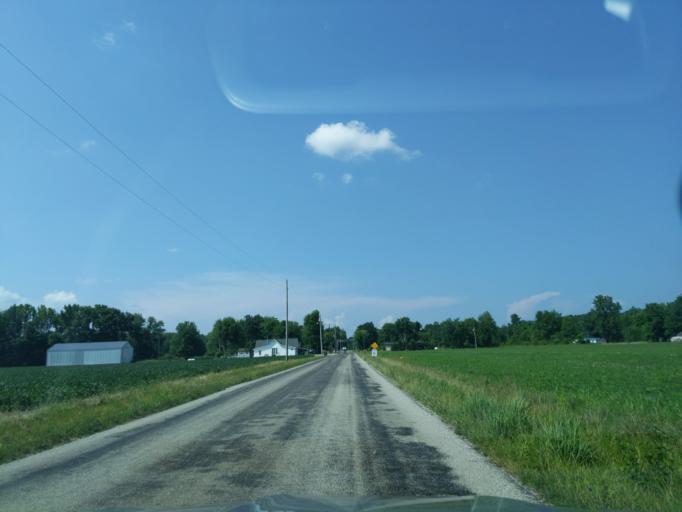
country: US
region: Indiana
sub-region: Ripley County
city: Osgood
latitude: 39.0872
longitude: -85.3470
